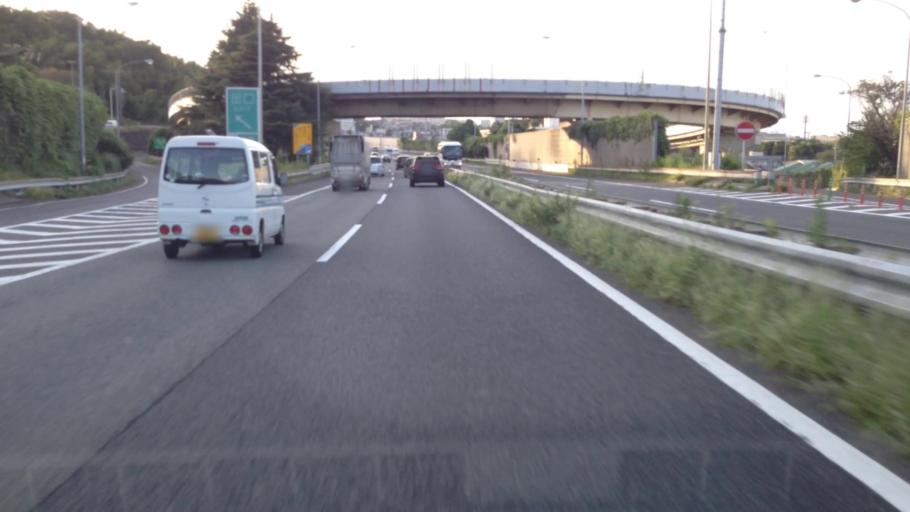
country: JP
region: Kanagawa
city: Kamakura
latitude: 35.3818
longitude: 139.5849
